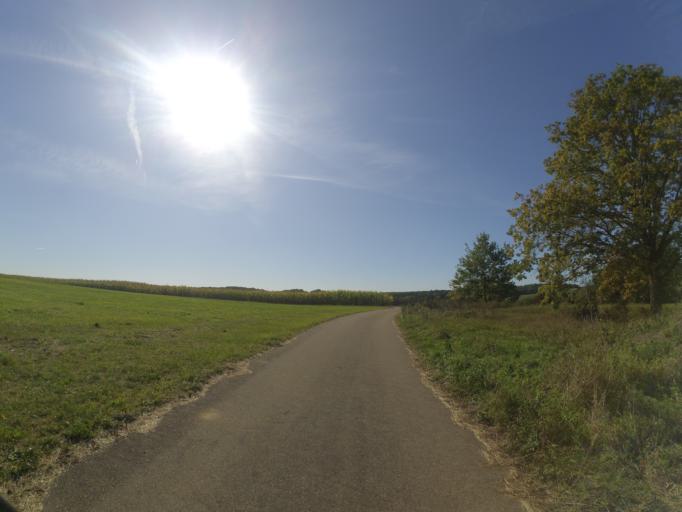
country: DE
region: Baden-Wuerttemberg
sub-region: Tuebingen Region
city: Ballendorf
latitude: 48.5471
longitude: 10.0853
